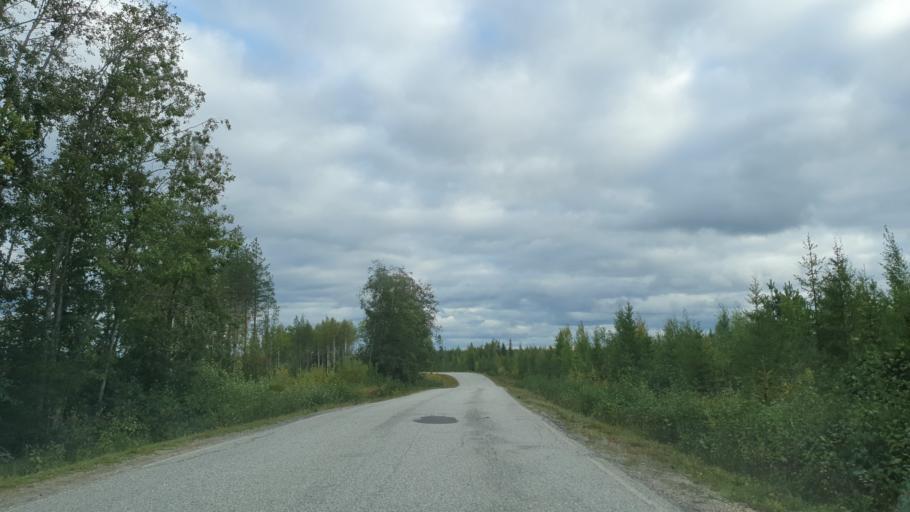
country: FI
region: Kainuu
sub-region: Kehys-Kainuu
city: Kuhmo
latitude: 63.9525
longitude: 29.7454
